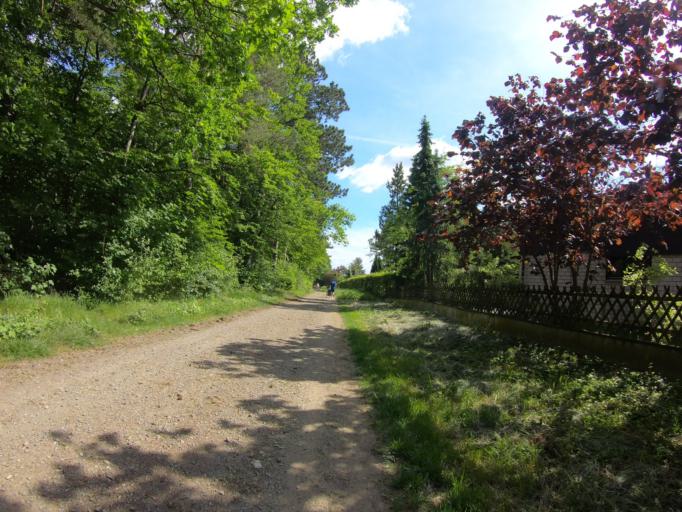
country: DE
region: Lower Saxony
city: Wolfenbuettel
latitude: 52.1851
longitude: 10.5290
